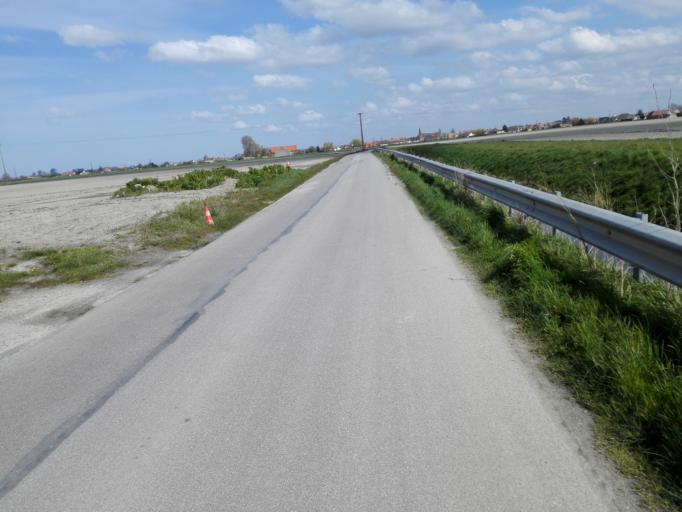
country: FR
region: Nord-Pas-de-Calais
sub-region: Departement du Nord
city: Spycker
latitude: 50.9662
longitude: 2.3087
